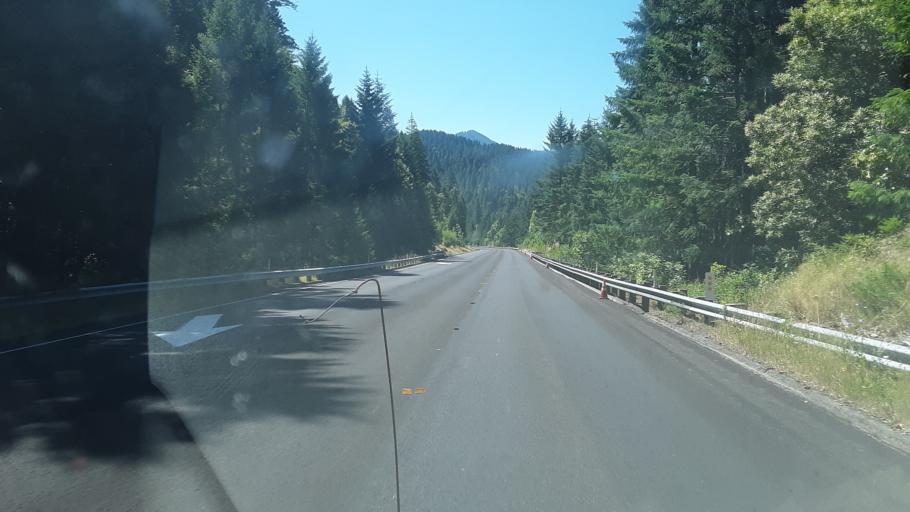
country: US
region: Oregon
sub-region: Josephine County
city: Cave Junction
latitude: 41.9624
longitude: -123.7469
